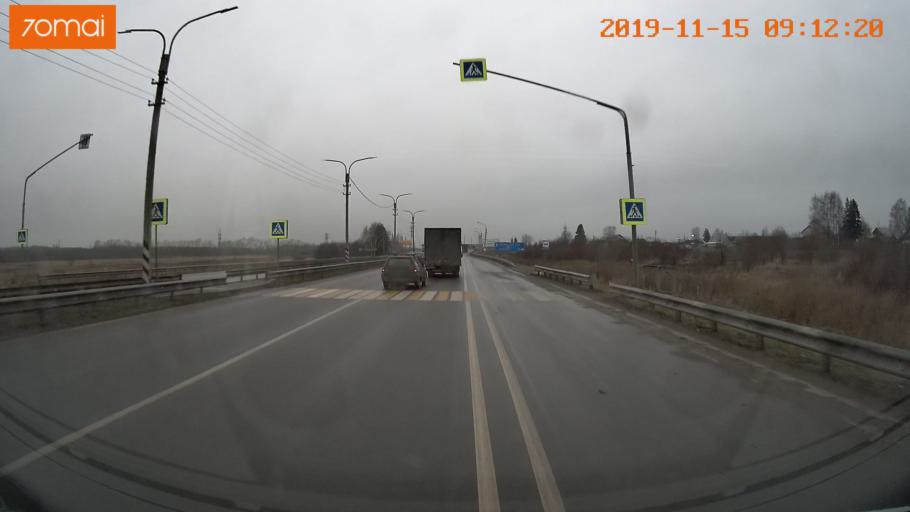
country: RU
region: Vologda
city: Tonshalovo
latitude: 59.2070
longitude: 37.9381
